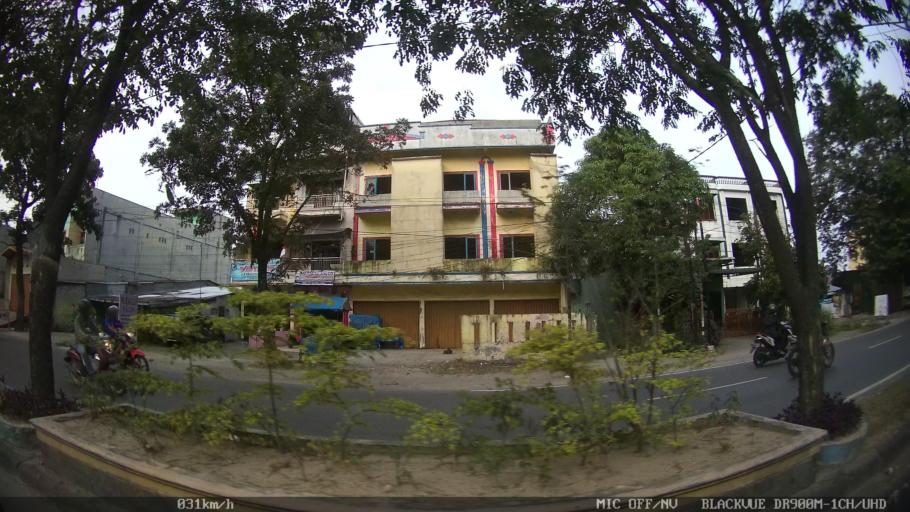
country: ID
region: North Sumatra
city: Sunggal
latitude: 3.5837
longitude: 98.6151
